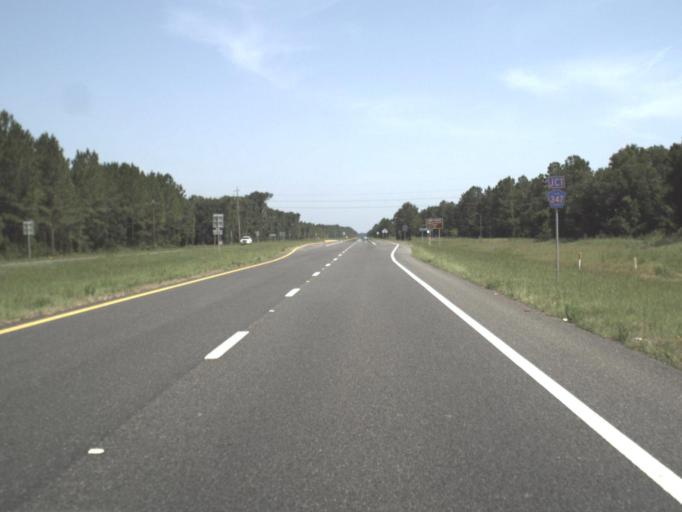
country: US
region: Florida
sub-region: Levy County
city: Chiefland
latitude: 29.4149
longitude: -82.8219
